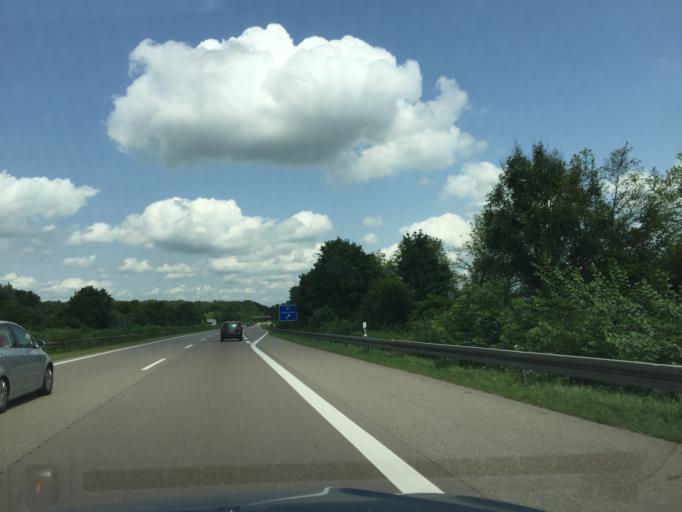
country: DE
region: Bavaria
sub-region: Swabia
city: Nersingen
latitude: 48.4264
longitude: 10.0986
